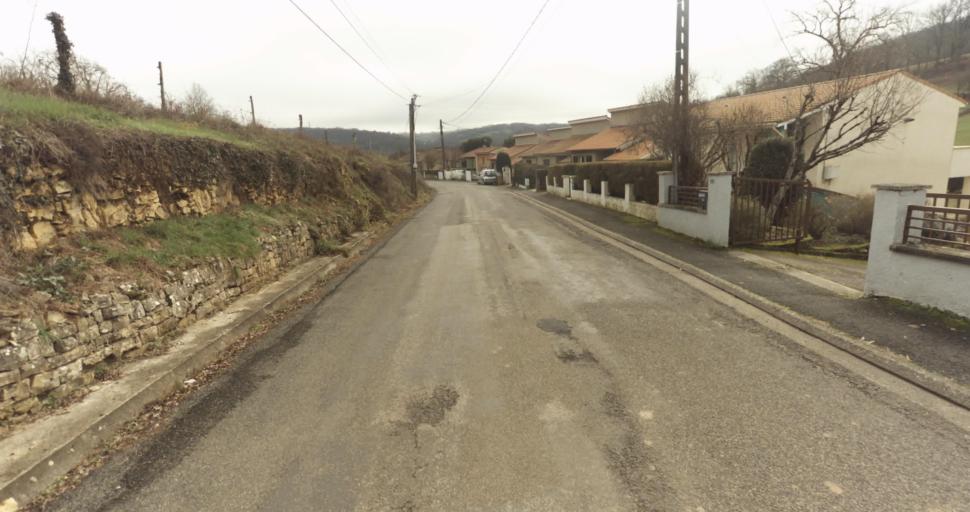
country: FR
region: Midi-Pyrenees
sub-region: Departement du Lot
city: Figeac
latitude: 44.6153
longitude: 2.0160
